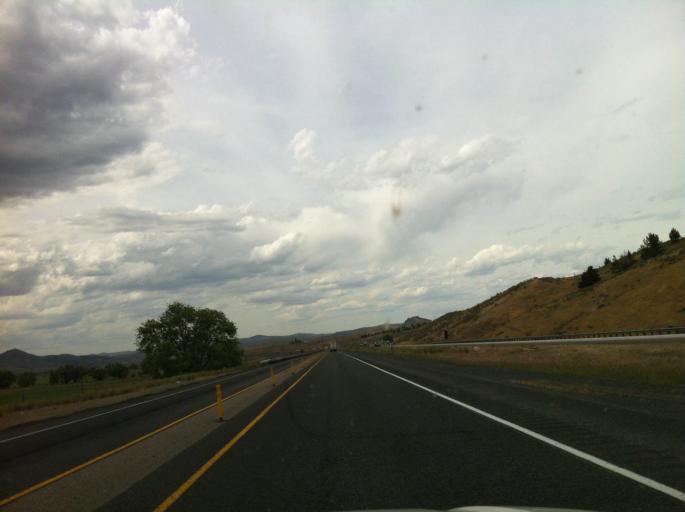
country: US
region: Oregon
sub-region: Baker County
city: Baker City
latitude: 44.5492
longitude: -117.4217
